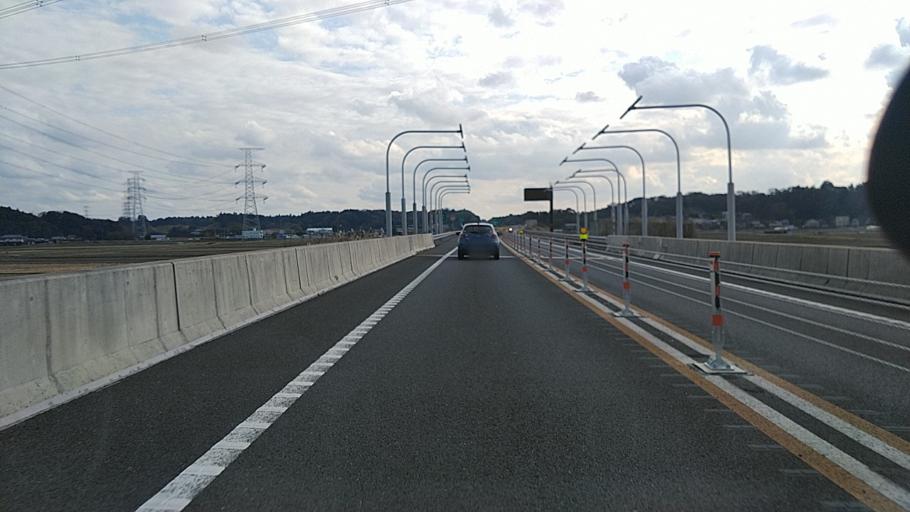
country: JP
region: Ibaraki
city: Inashiki
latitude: 35.8912
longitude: 140.3812
